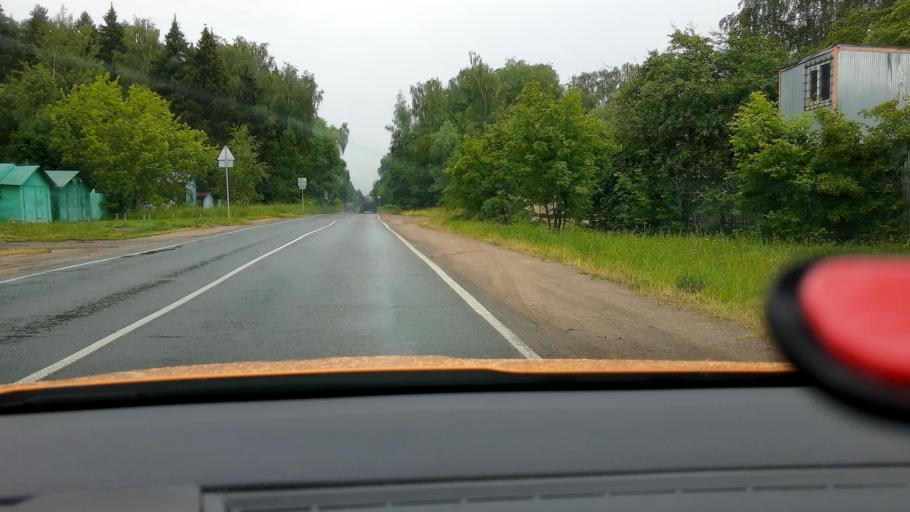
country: RU
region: Moskovskaya
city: Pirogovskiy
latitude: 55.9962
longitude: 37.6725
